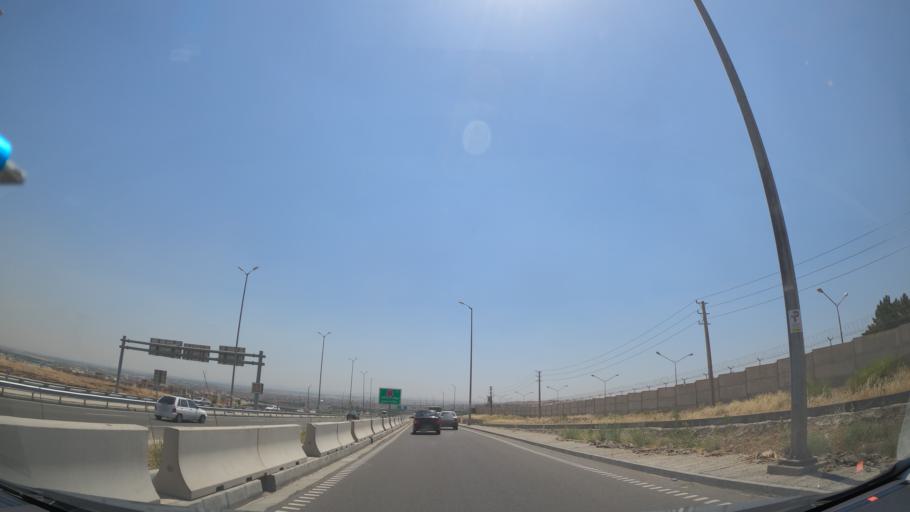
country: IR
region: Tehran
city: Shahr-e Qods
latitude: 35.7484
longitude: 51.1305
